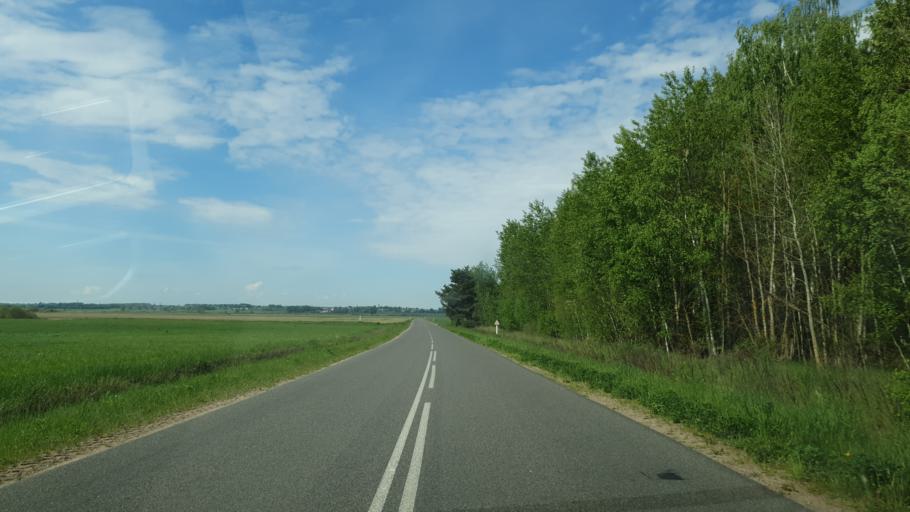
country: BY
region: Grodnenskaya
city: Mir
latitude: 53.4224
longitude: 26.3606
